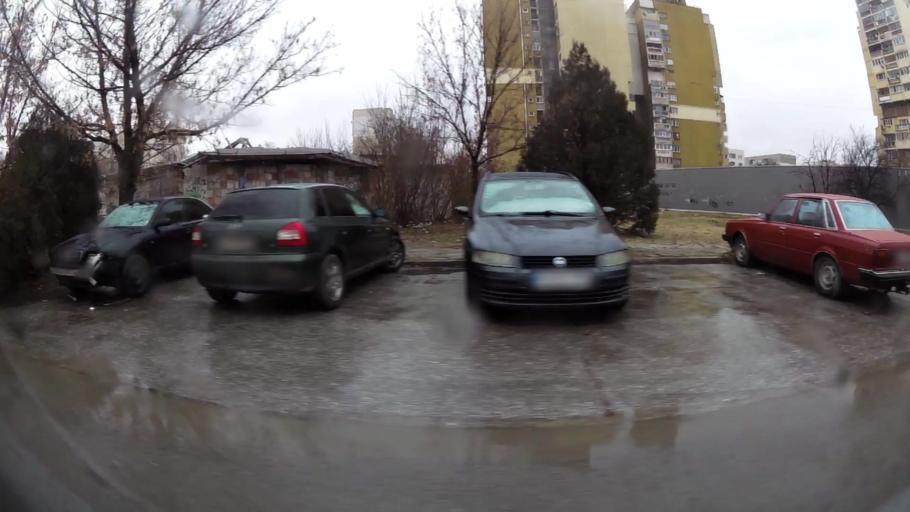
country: BG
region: Sofia-Capital
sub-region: Stolichna Obshtina
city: Sofia
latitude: 42.6615
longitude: 23.3984
